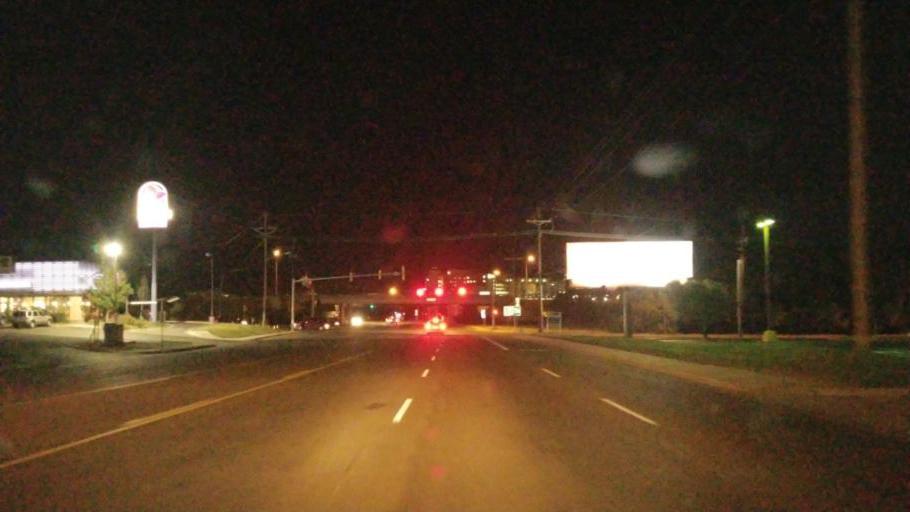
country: US
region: Texas
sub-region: Potter County
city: Amarillo
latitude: 35.1904
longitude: -101.9203
